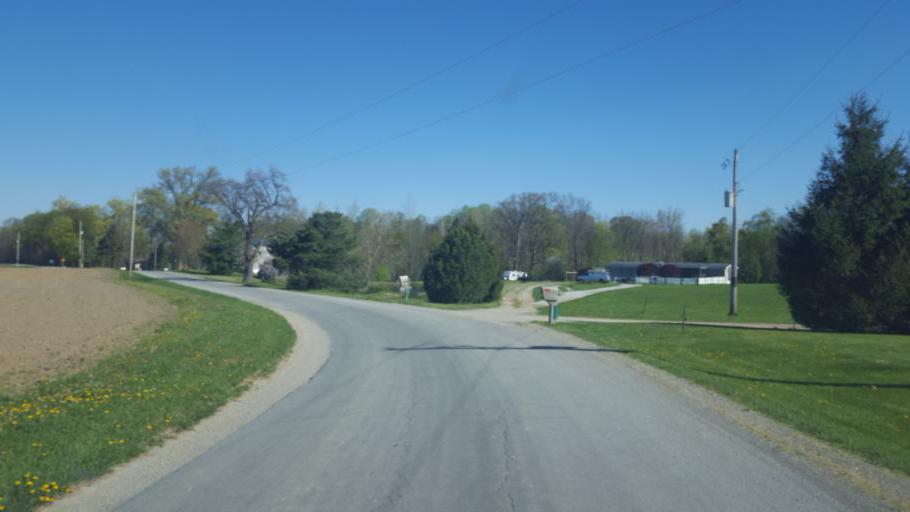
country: US
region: Ohio
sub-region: Wyandot County
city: Upper Sandusky
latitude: 40.8991
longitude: -83.2214
